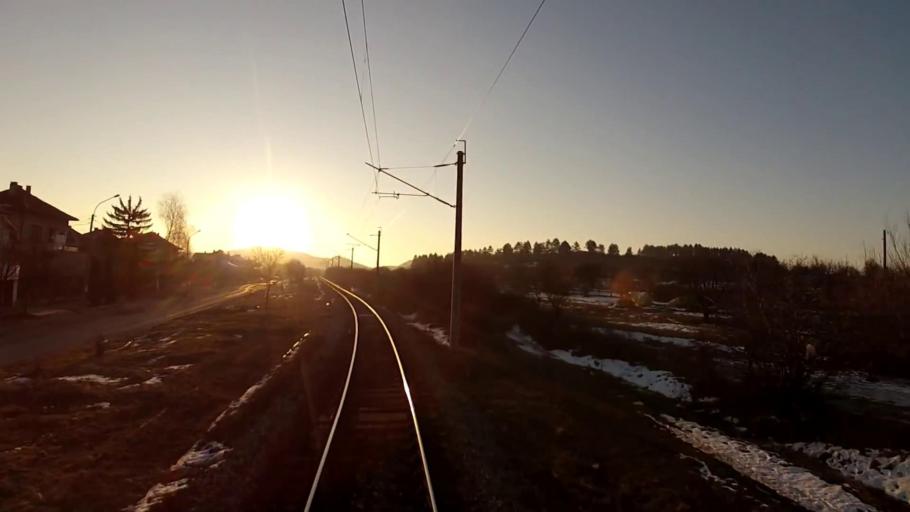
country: BG
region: Sofiya
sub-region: Obshtina Dragoman
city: Dragoman
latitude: 42.9138
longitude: 22.9380
